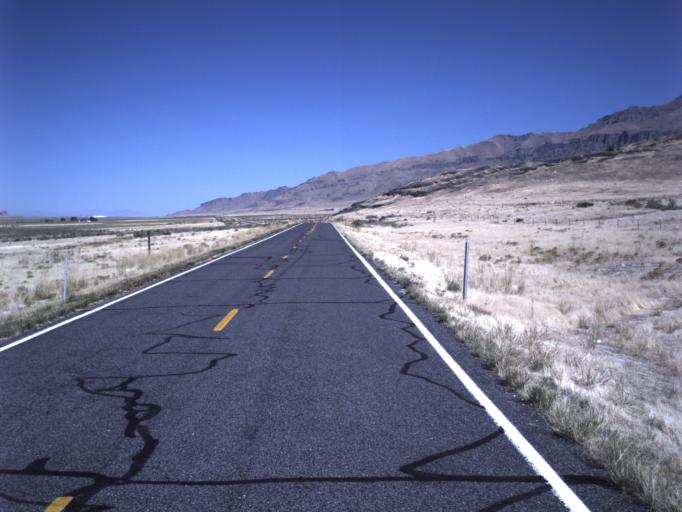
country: US
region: Utah
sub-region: Tooele County
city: Grantsville
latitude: 40.6077
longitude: -112.7081
